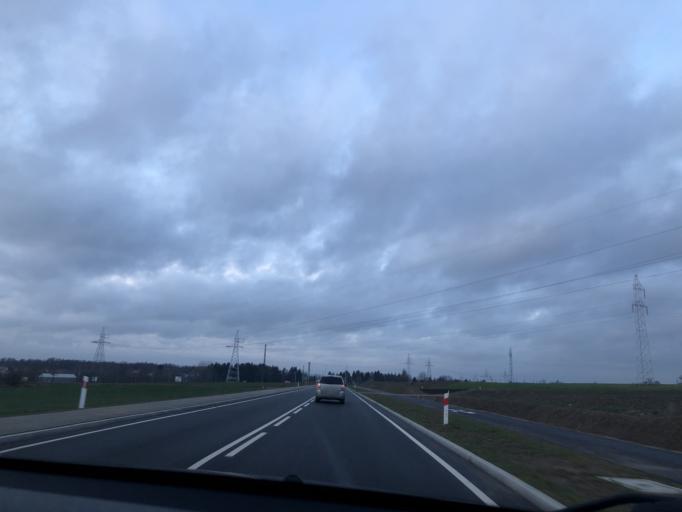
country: PL
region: Podlasie
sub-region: Lomza
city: Lomza
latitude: 53.1475
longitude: 22.0524
